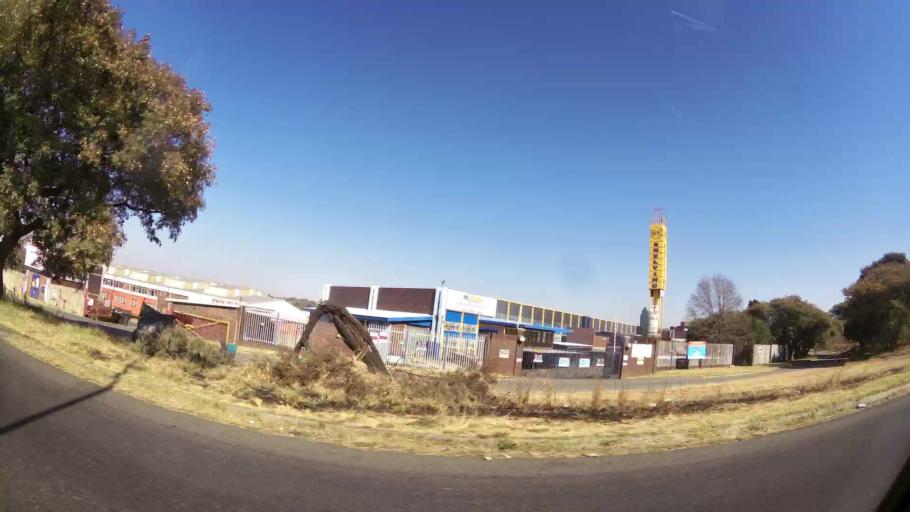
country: ZA
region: Gauteng
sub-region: Ekurhuleni Metropolitan Municipality
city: Germiston
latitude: -26.2492
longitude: 28.1075
